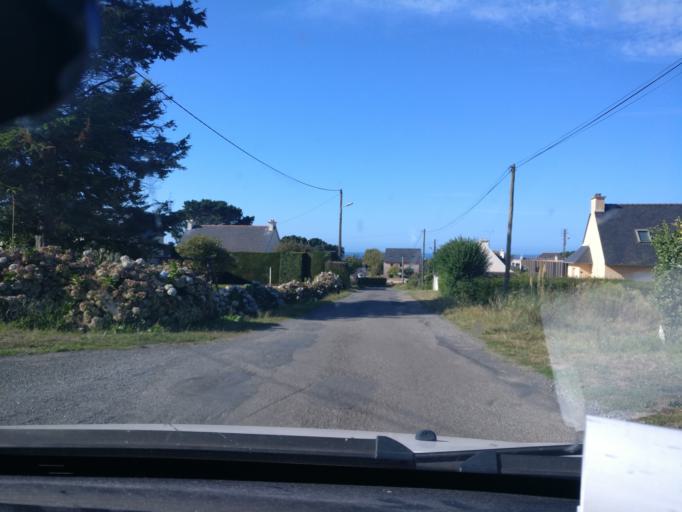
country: FR
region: Brittany
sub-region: Departement des Cotes-d'Armor
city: Trelevern
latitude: 48.8131
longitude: -3.3693
